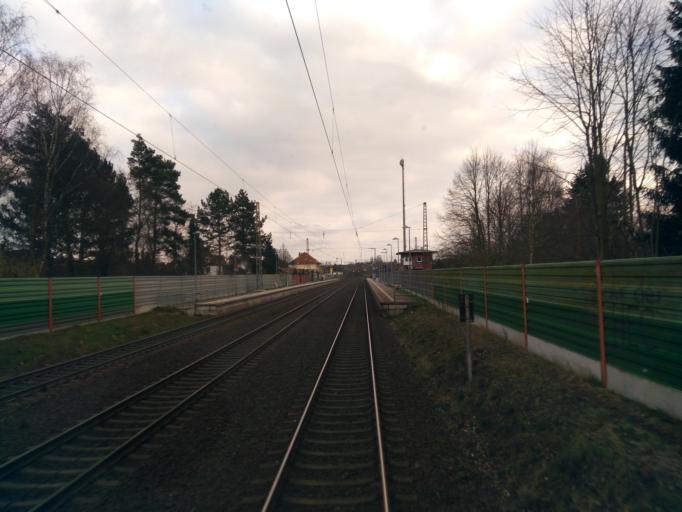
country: DE
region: Lower Saxony
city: Bienenbuttel
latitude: 53.1434
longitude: 10.4828
